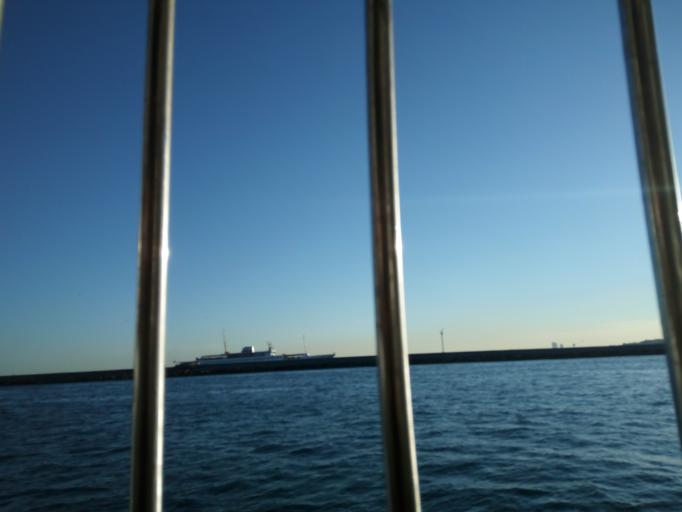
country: TR
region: Istanbul
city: UEskuedar
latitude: 41.0053
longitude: 29.0070
